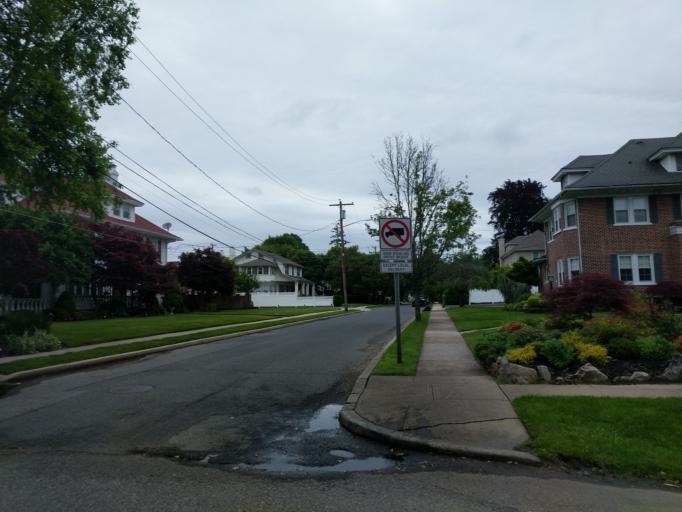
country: US
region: New York
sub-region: Nassau County
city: Woodmere
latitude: 40.6277
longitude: -73.7086
